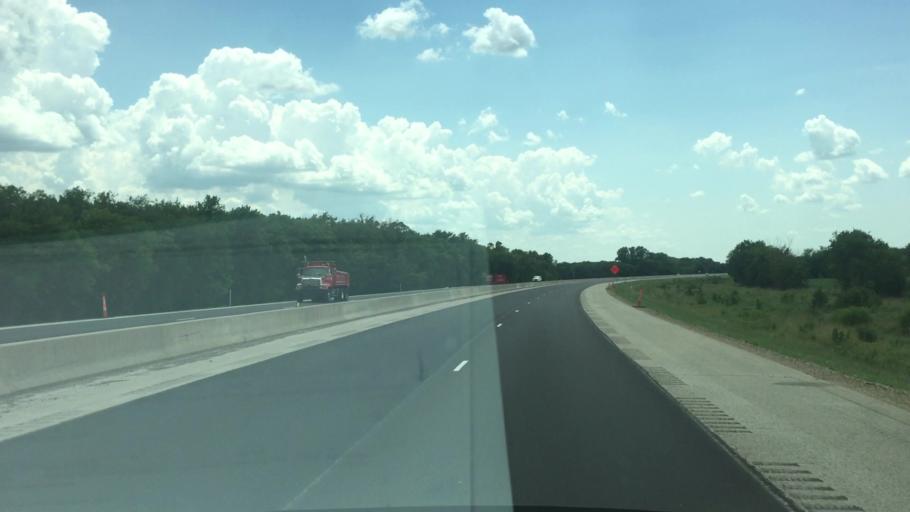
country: US
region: Kansas
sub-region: Lyon County
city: Emporia
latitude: 38.5021
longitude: -96.1524
